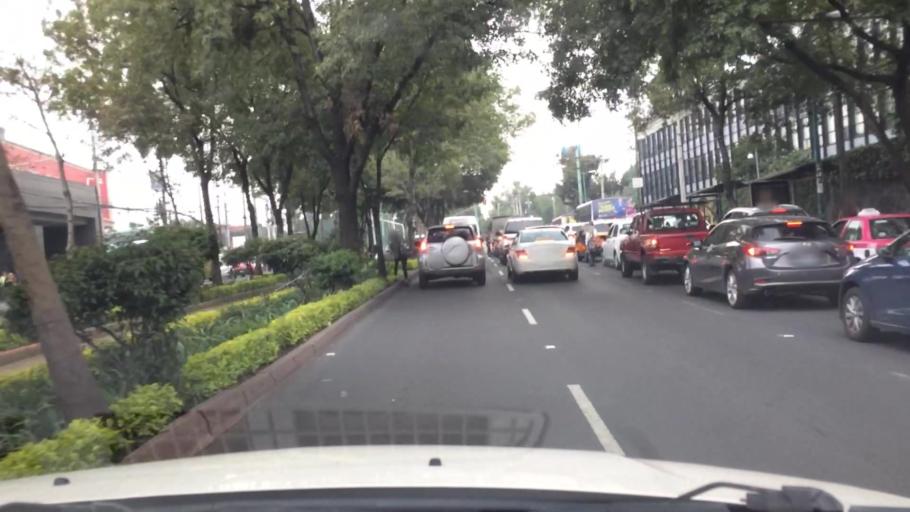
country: MX
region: Mexico City
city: Coyoacan
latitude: 19.3467
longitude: -99.1795
